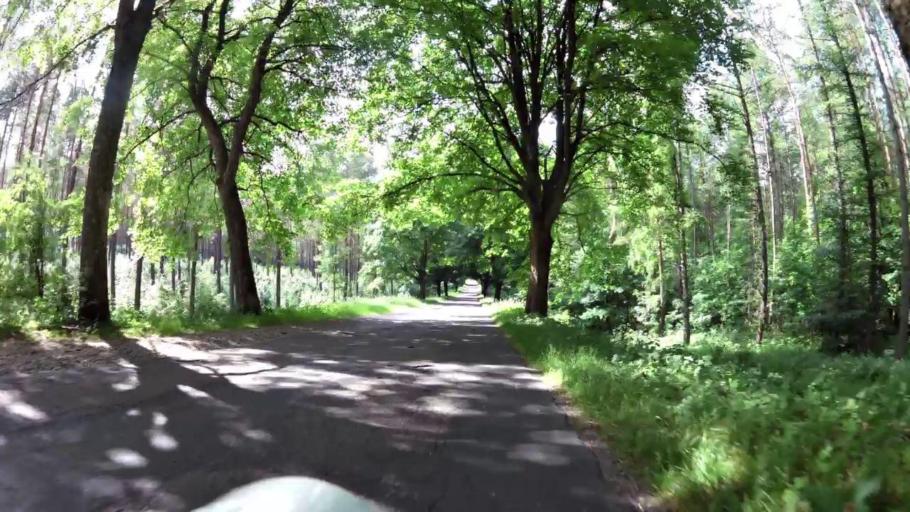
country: PL
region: West Pomeranian Voivodeship
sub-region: Powiat szczecinecki
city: Bialy Bor
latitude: 53.9553
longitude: 16.7539
